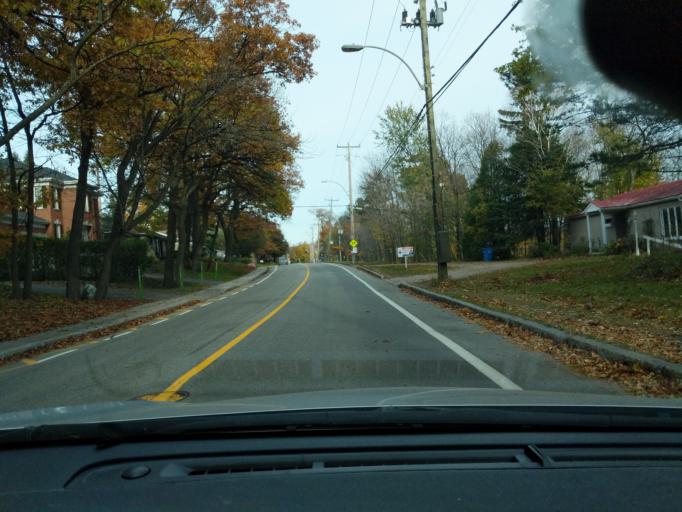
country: CA
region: Quebec
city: Quebec
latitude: 46.7699
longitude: -71.2629
